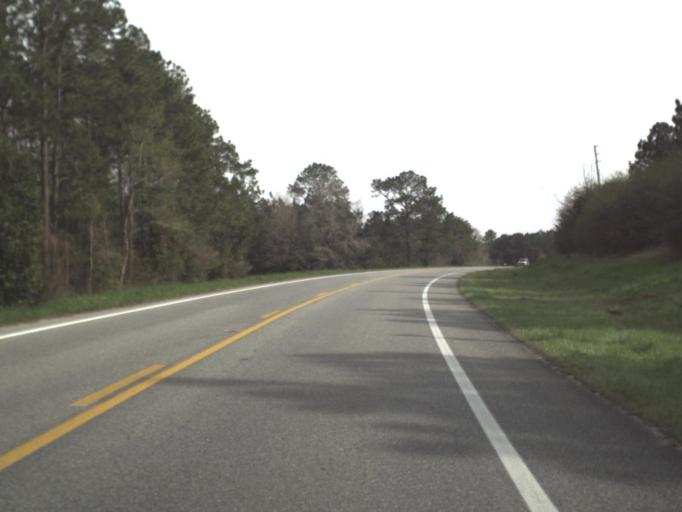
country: US
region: Florida
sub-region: Jefferson County
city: Monticello
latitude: 30.5351
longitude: -83.8311
